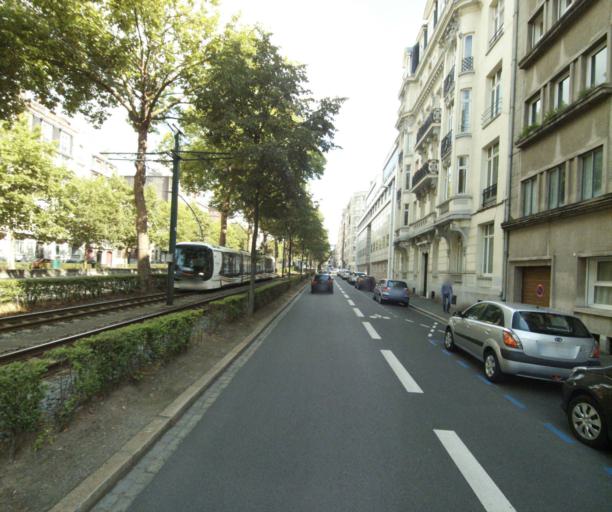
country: FR
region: Nord-Pas-de-Calais
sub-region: Departement du Nord
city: La Madeleine
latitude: 50.6477
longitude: 3.0776
